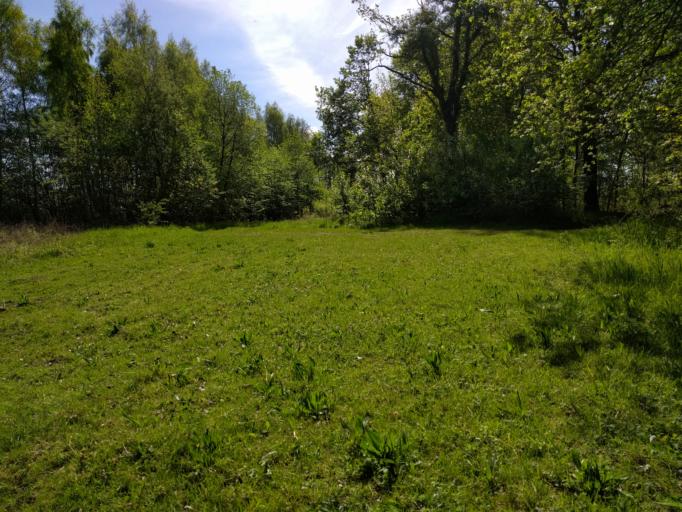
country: DK
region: South Denmark
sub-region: Kerteminde Kommune
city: Langeskov
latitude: 55.3878
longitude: 10.5602
